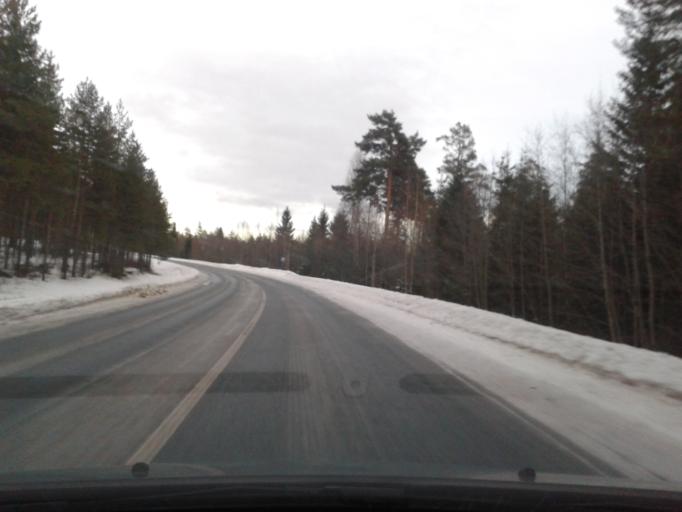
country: SE
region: Vaesternorrland
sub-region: Solleftea Kommun
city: Solleftea
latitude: 63.3324
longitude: 17.1001
